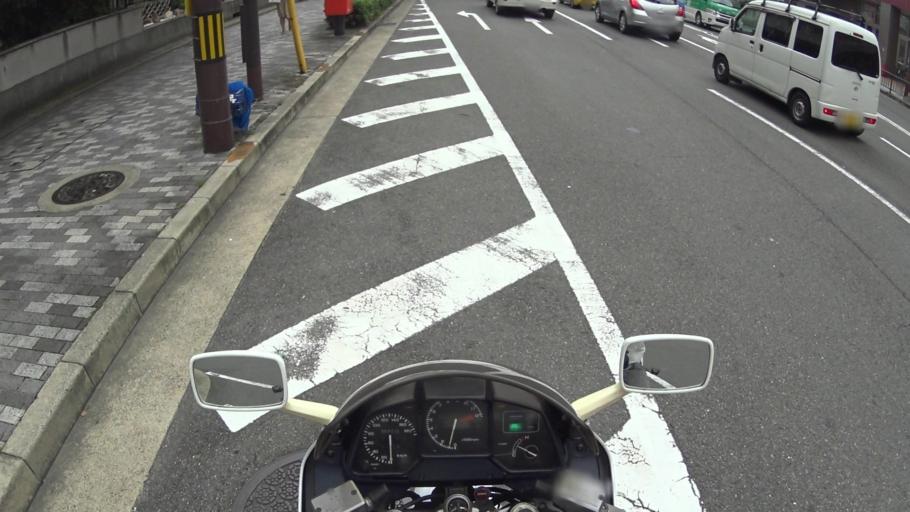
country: JP
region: Kyoto
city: Kyoto
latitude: 35.0131
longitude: 135.7427
